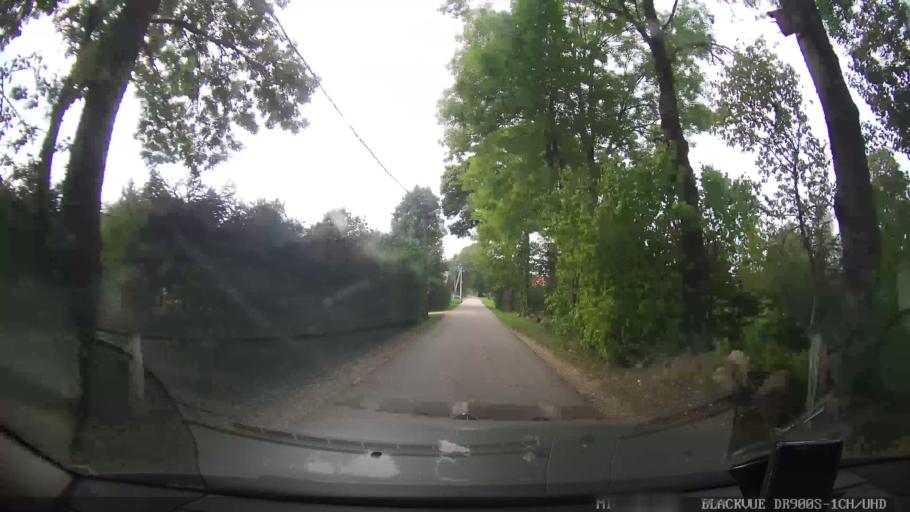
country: LT
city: Skaidiskes
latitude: 54.5330
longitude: 25.6644
